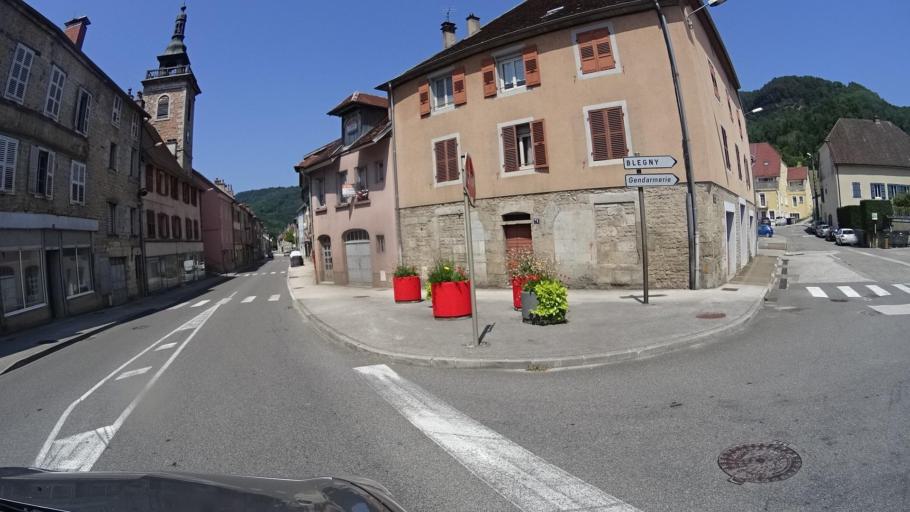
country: FR
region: Franche-Comte
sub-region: Departement du Jura
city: Salins-les-Bains
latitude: 46.9288
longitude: 5.8866
